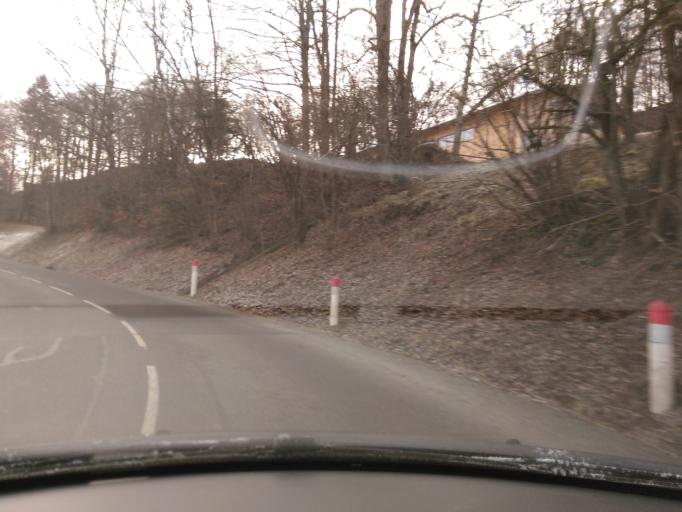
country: FR
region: Rhone-Alpes
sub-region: Departement de la Haute-Savoie
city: Cordon
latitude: 45.9287
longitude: 6.6110
